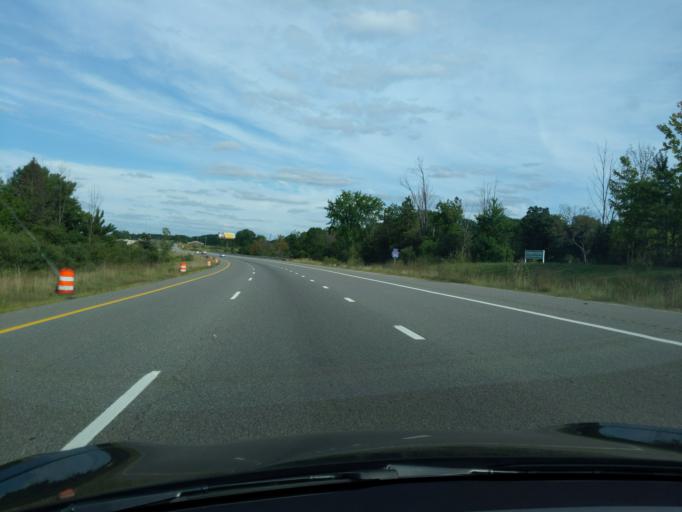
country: US
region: Michigan
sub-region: Muskegon County
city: Fruitport
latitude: 43.0720
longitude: -86.0758
